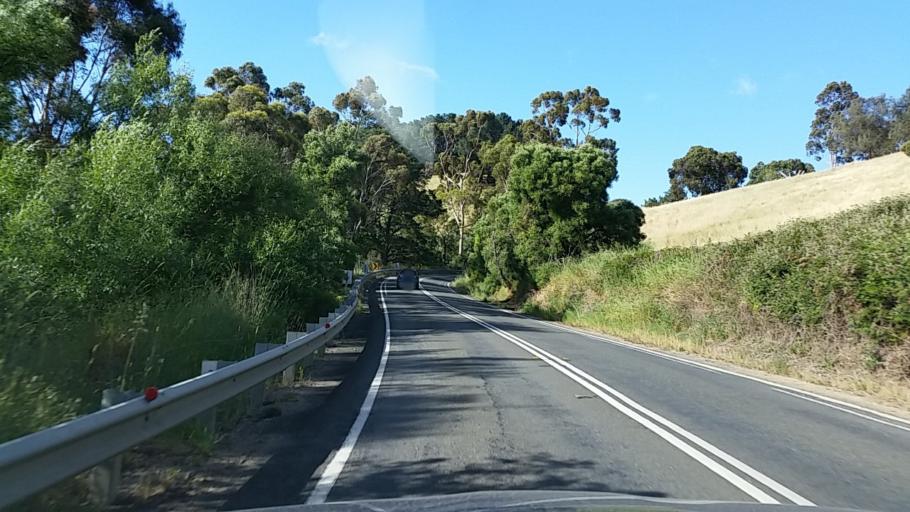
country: AU
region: South Australia
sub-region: Mount Barker
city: Meadows
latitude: -35.2375
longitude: 138.7656
